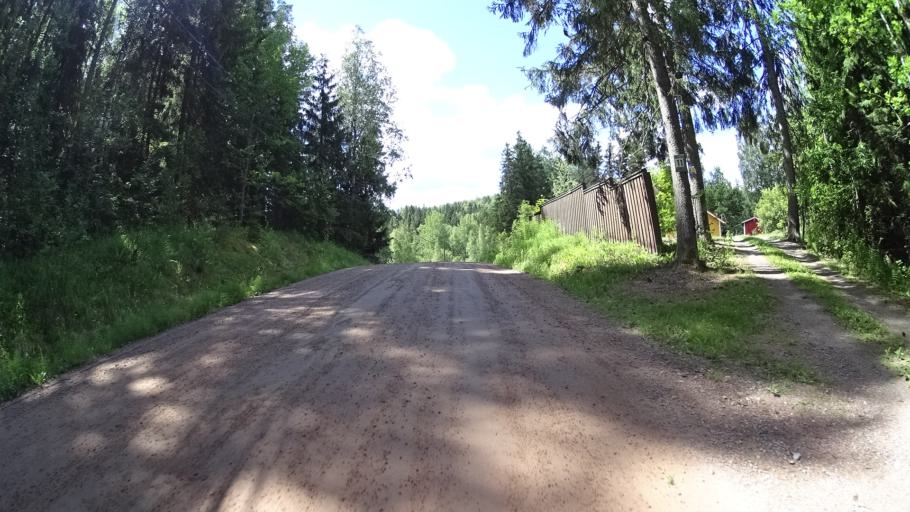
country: FI
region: Uusimaa
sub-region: Helsinki
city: Espoo
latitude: 60.3078
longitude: 24.5395
